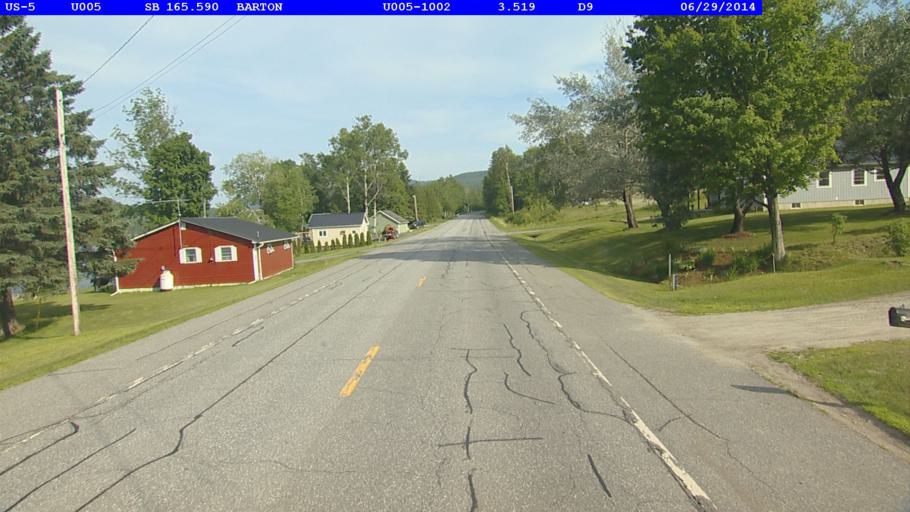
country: US
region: Vermont
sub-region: Orleans County
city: Newport
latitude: 44.7264
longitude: -72.1538
